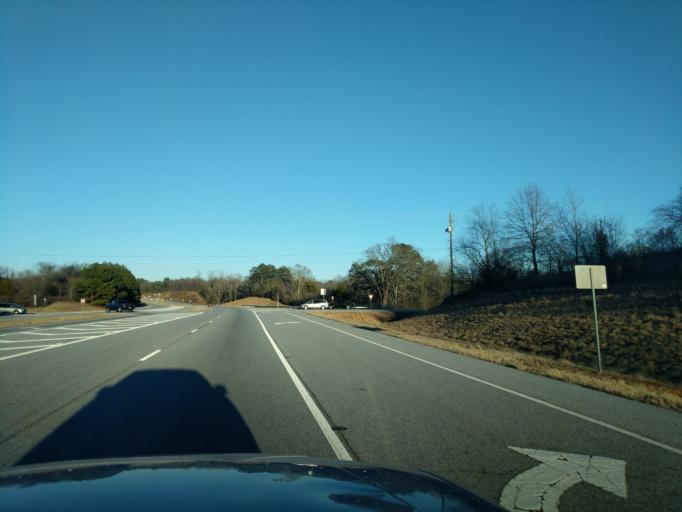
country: US
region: Georgia
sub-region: Stephens County
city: Toccoa
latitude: 34.5438
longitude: -83.2859
